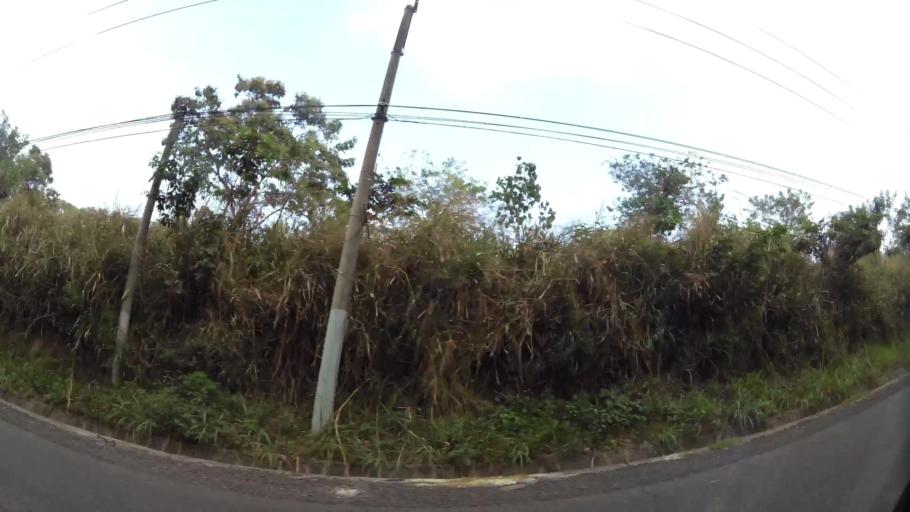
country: SV
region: San Salvador
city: Delgado
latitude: 13.7201
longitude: -89.1571
